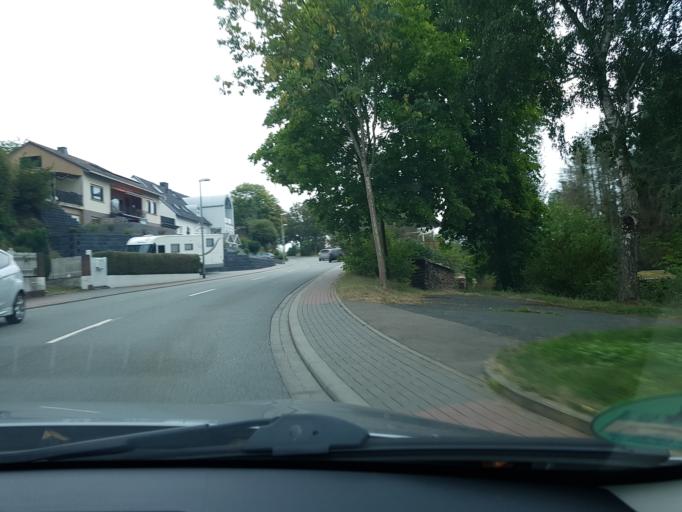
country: DE
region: Rheinland-Pfalz
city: Hainau
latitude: 50.2233
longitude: 7.7824
